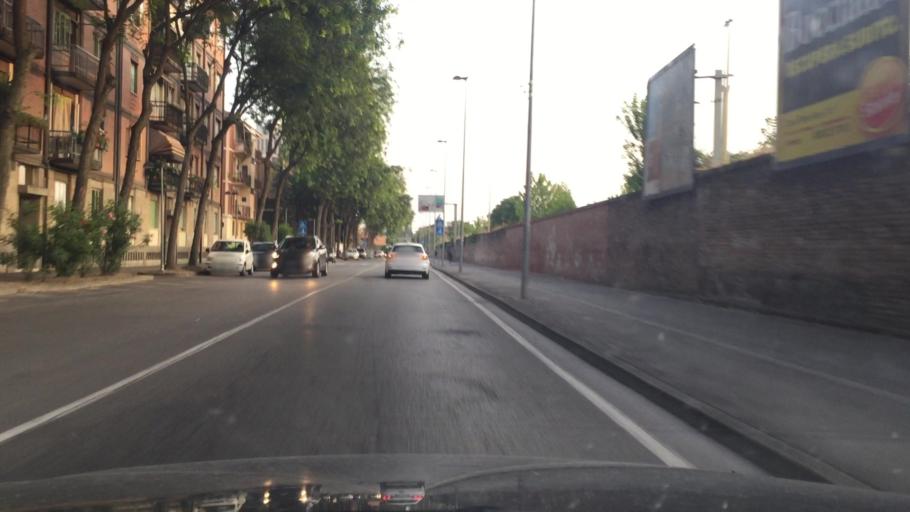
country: IT
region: Emilia-Romagna
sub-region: Provincia di Ferrara
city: Ferrara
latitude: 44.8412
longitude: 11.6032
